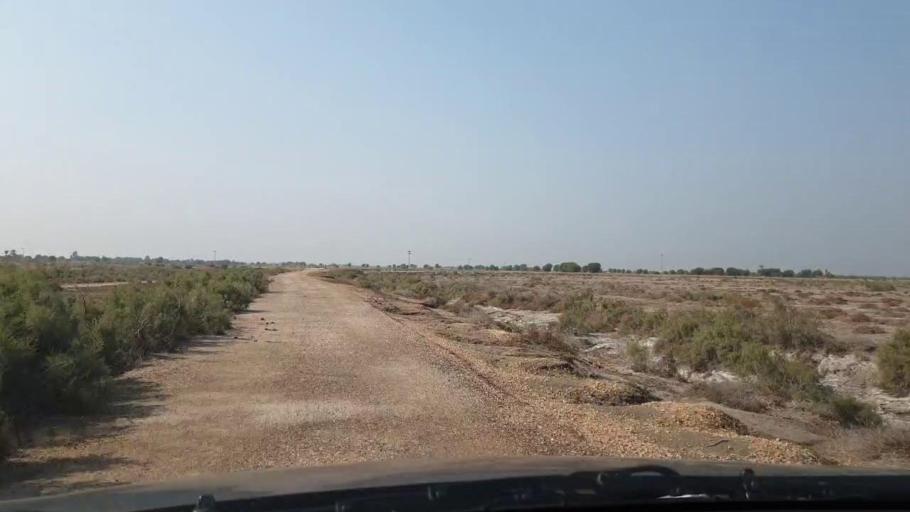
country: PK
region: Sindh
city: Jhol
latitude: 25.8921
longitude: 68.9603
